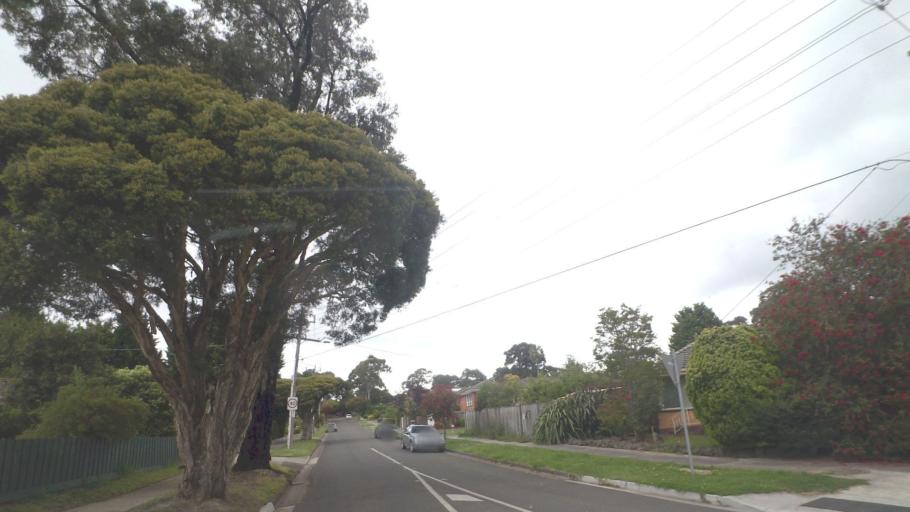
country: AU
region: Victoria
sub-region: Knox
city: Bayswater
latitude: -37.8540
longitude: 145.2596
